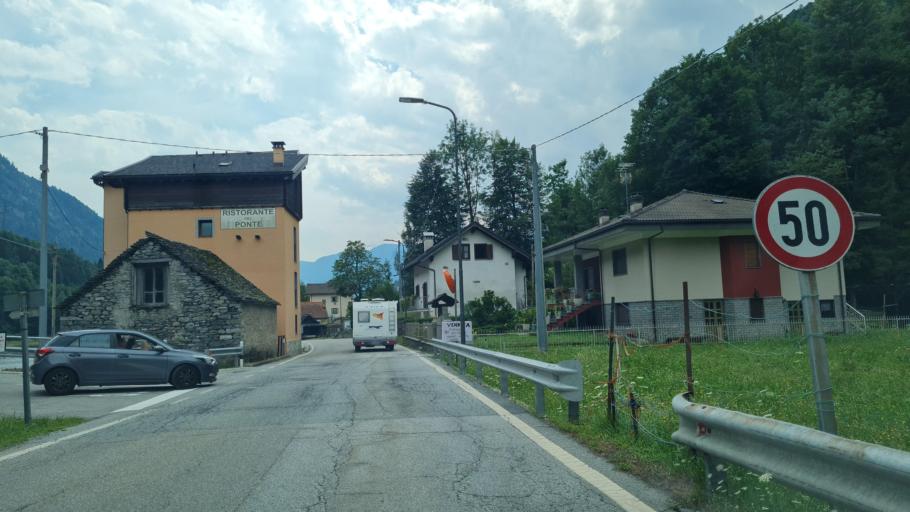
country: IT
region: Piedmont
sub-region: Provincia Verbano-Cusio-Ossola
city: Premia
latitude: 46.2804
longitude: 8.3531
